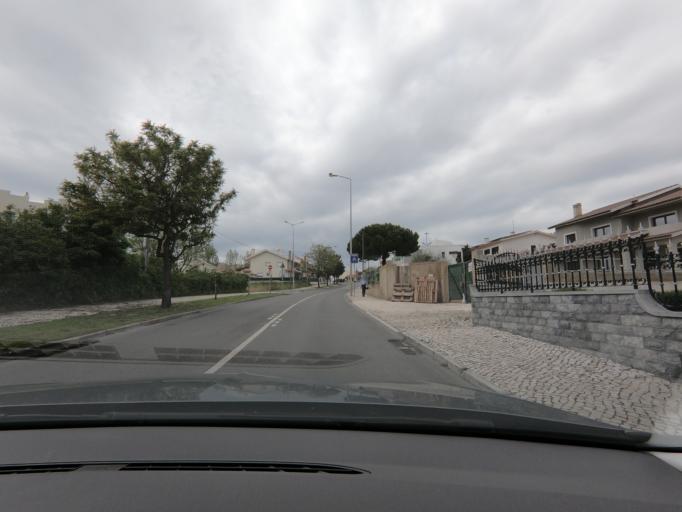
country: PT
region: Lisbon
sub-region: Cascais
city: Sao Domingos de Rana
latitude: 38.6997
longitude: -9.3367
